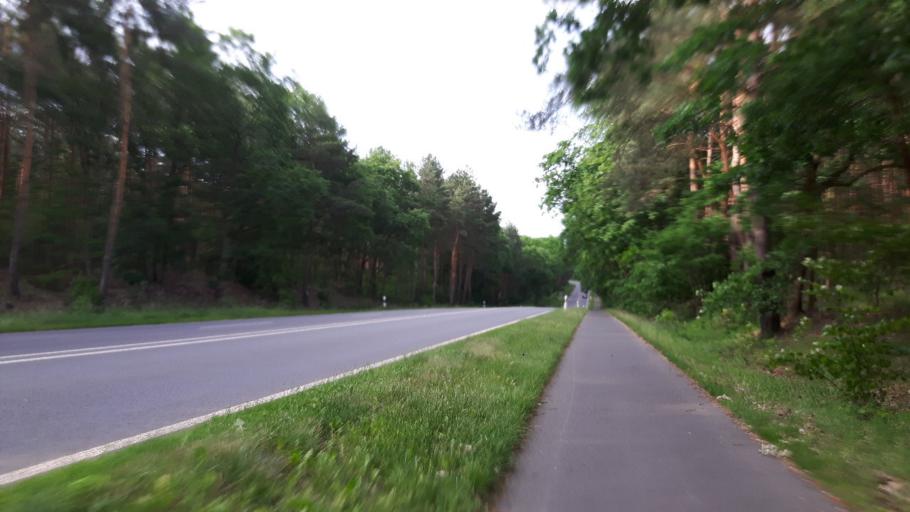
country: DE
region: Brandenburg
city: Potsdam
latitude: 52.3710
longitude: 13.0502
